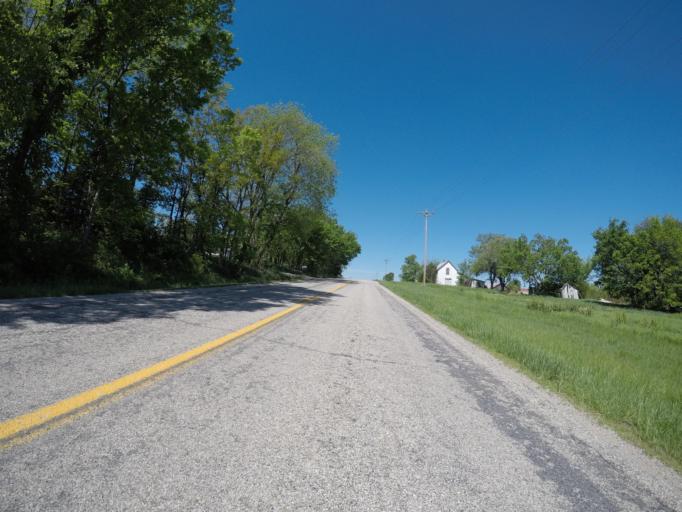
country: US
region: Kansas
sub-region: Osage County
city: Overbrook
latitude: 38.8405
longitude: -95.5498
